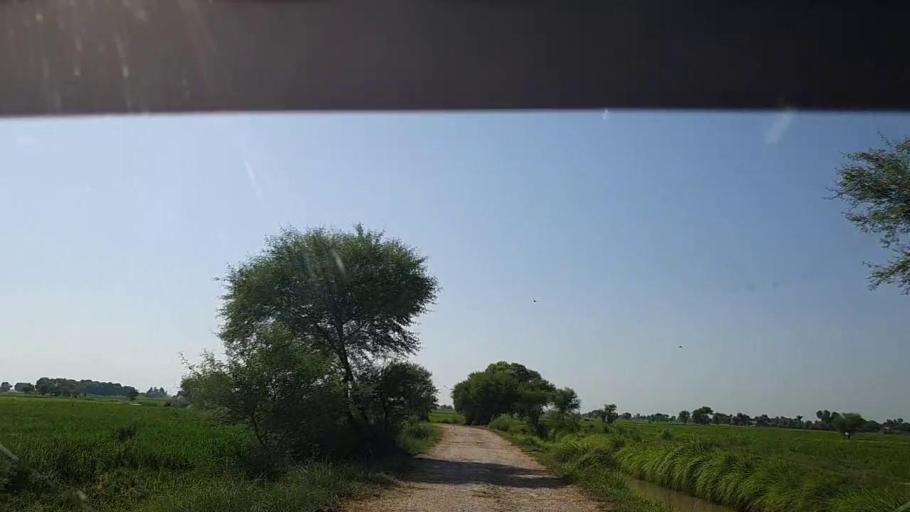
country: PK
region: Sindh
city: Ghauspur
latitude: 28.1785
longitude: 69.0372
